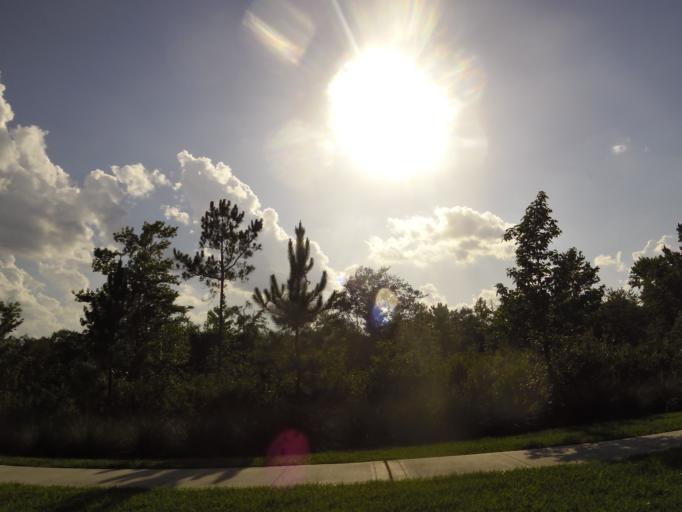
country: US
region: Florida
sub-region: Clay County
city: Green Cove Springs
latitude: 30.0334
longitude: -81.6255
